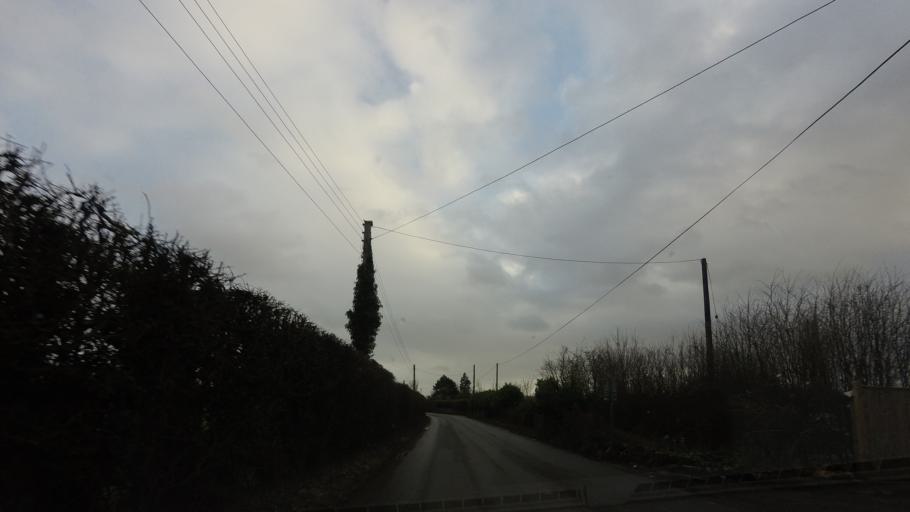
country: GB
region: England
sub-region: Kent
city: Yalding
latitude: 51.2268
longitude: 0.4073
